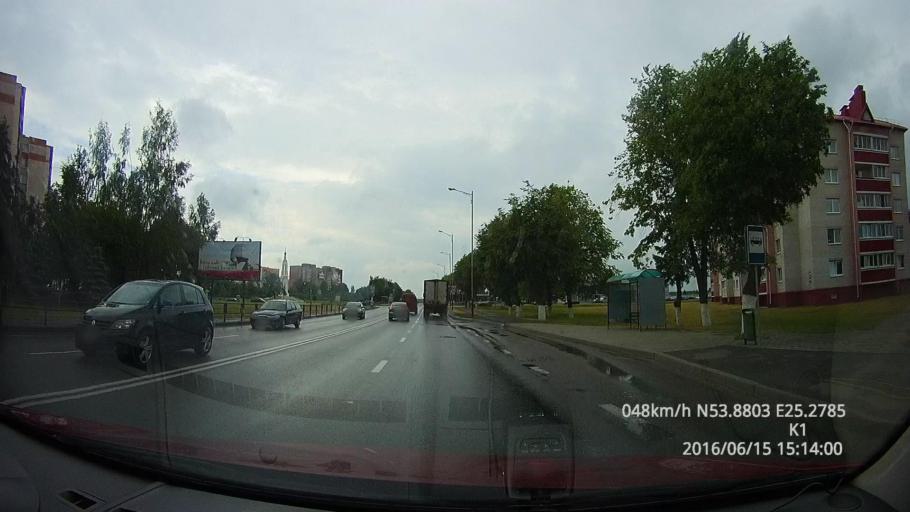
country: BY
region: Grodnenskaya
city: Lida
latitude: 53.8801
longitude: 25.2783
